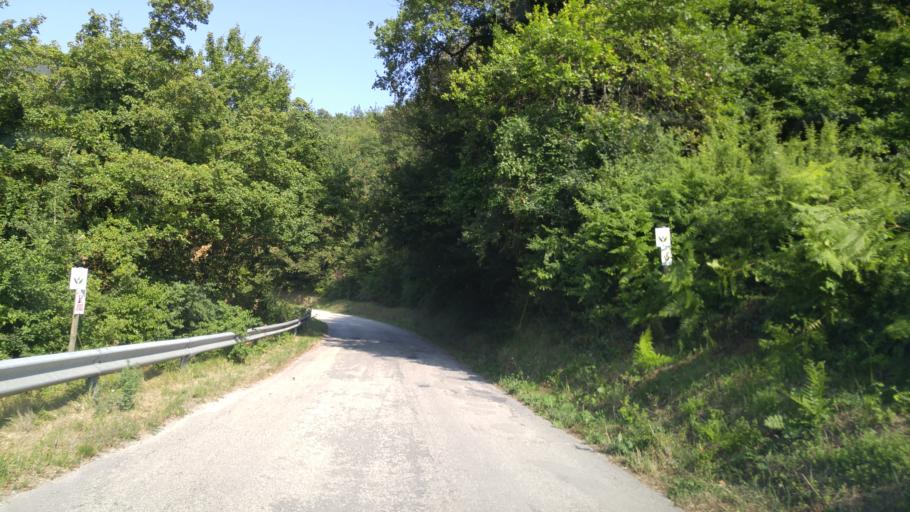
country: IT
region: The Marches
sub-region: Provincia di Pesaro e Urbino
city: Acqualagna
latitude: 43.6338
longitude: 12.7067
